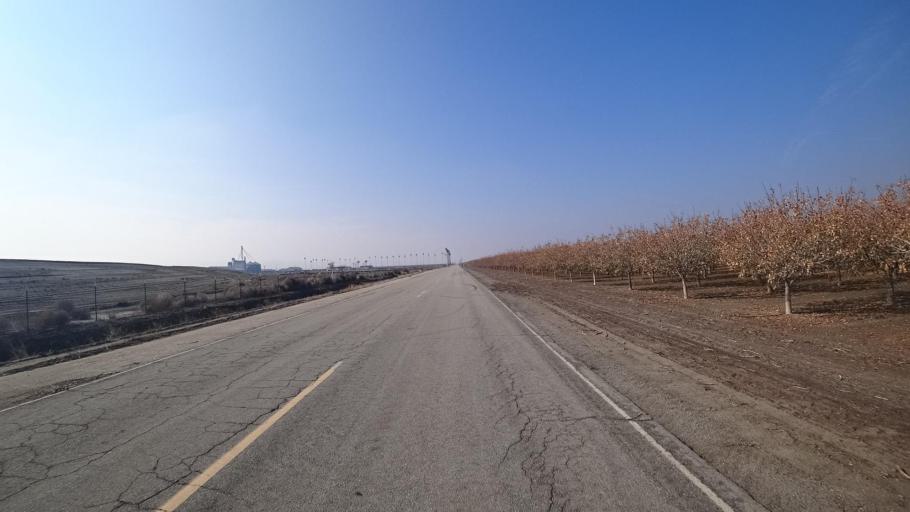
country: US
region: California
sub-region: Kern County
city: Buttonwillow
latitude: 35.3403
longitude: -119.3861
